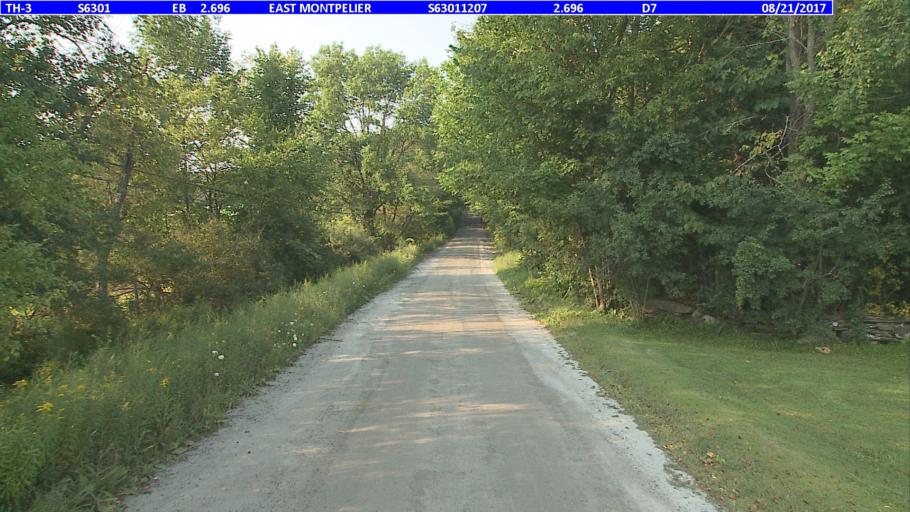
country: US
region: Vermont
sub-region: Washington County
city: Montpelier
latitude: 44.2968
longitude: -72.5171
